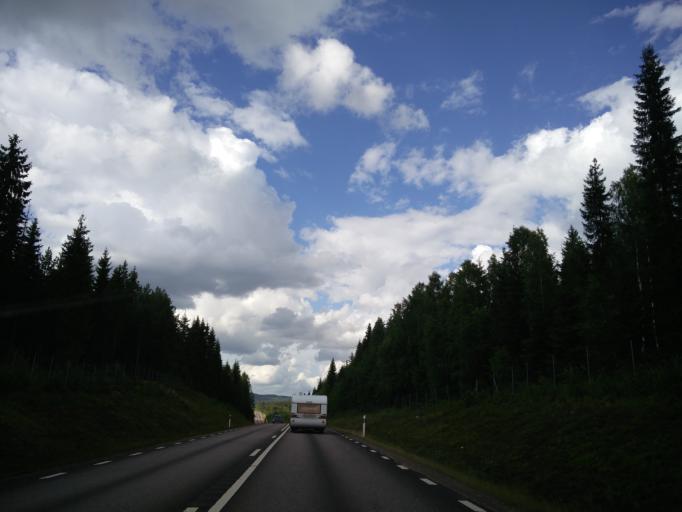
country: SE
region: Vaermland
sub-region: Torsby Kommun
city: Torsby
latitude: 60.1807
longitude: 13.0124
